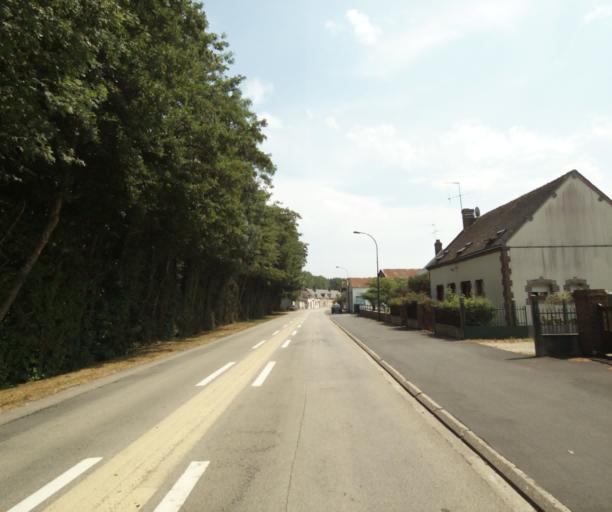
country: FR
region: Centre
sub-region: Departement d'Eure-et-Loir
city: Unverre
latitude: 48.1952
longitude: 1.0881
